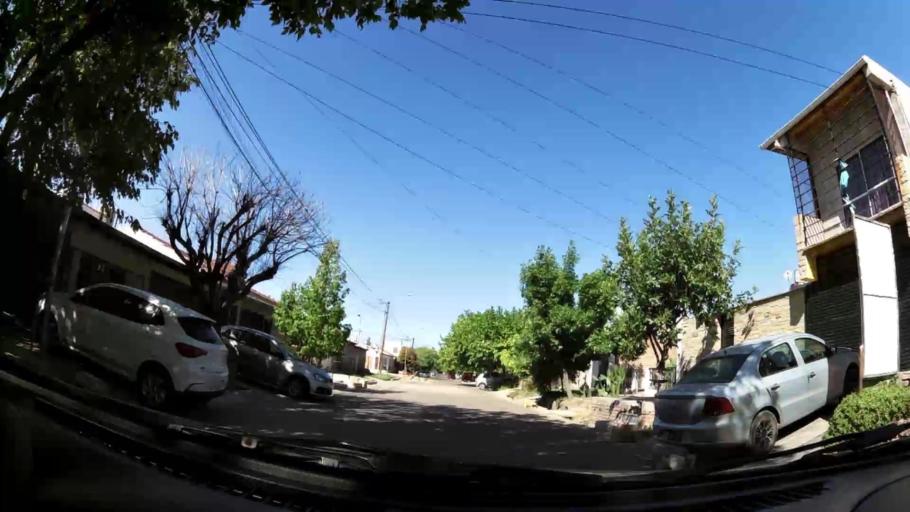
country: AR
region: Mendoza
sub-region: Departamento de Godoy Cruz
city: Godoy Cruz
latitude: -32.9490
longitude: -68.8178
